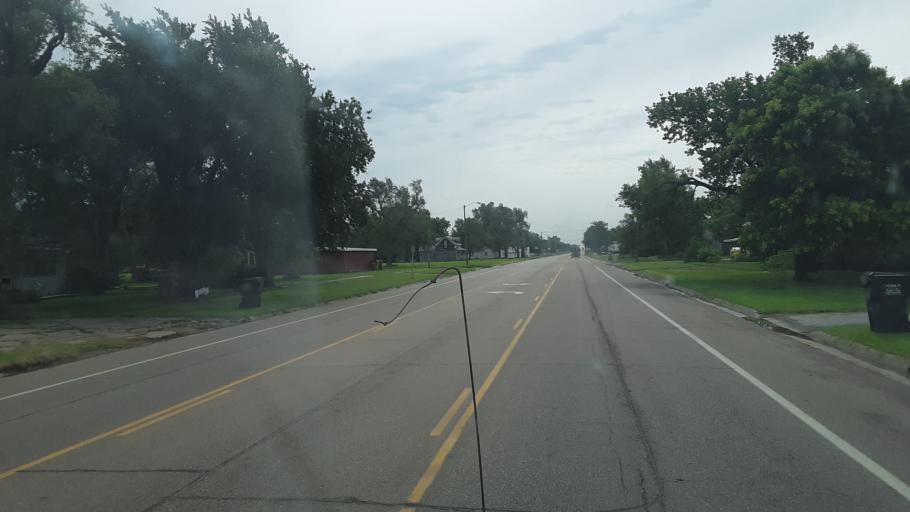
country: US
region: Kansas
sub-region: Stafford County
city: Saint John
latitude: 37.9566
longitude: -98.9718
